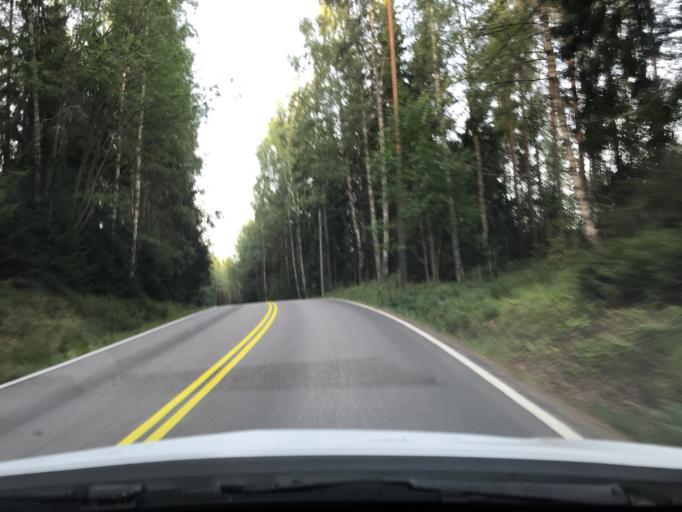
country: FI
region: Uusimaa
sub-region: Helsinki
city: Vihti
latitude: 60.4159
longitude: 24.4743
